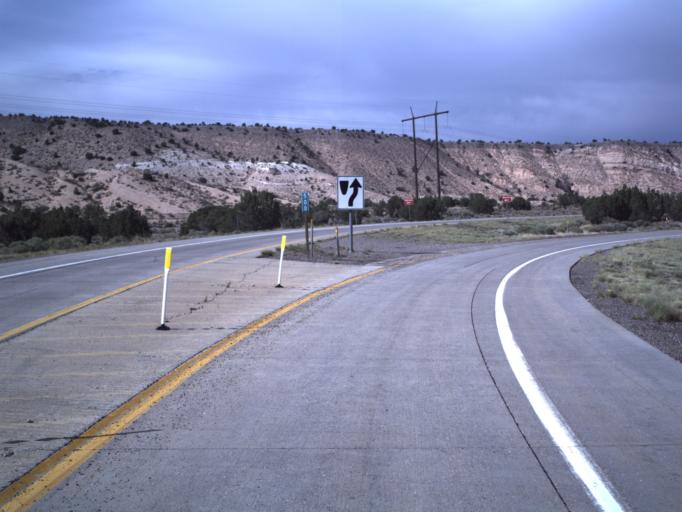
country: US
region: Utah
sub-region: Sevier County
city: Monroe
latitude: 38.6016
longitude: -112.2545
